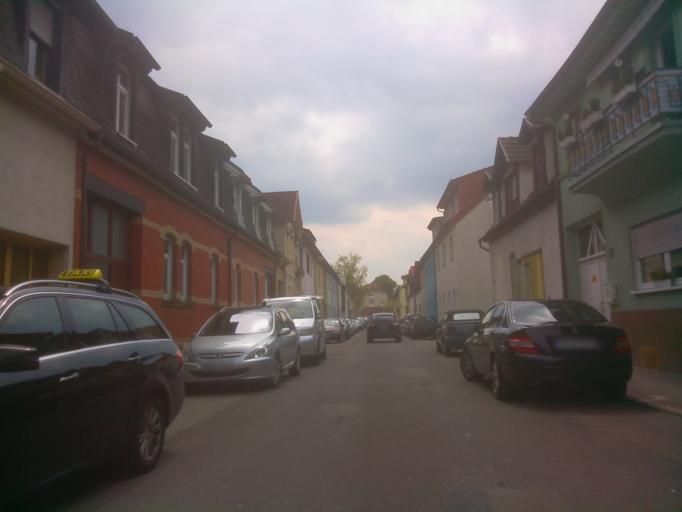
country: DE
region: Baden-Wuerttemberg
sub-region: Karlsruhe Region
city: Plankstadt
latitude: 49.3946
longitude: 8.5943
